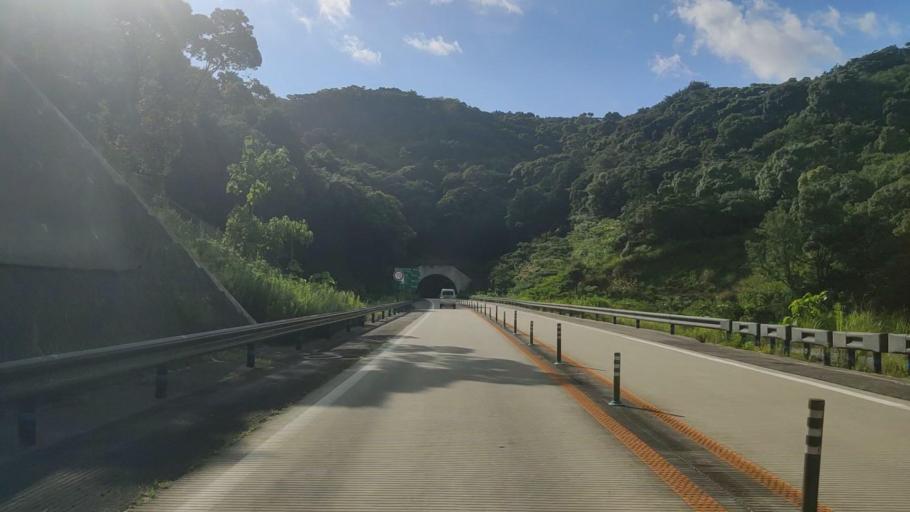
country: JP
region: Wakayama
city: Tanabe
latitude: 33.5855
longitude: 135.4479
